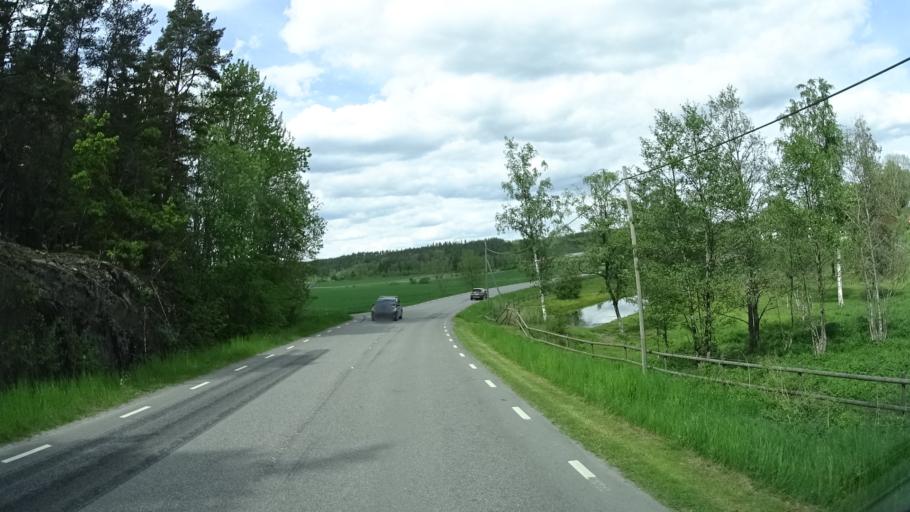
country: SE
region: OEstergoetland
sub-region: Norrkopings Kommun
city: Skarblacka
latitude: 58.5923
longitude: 15.8383
